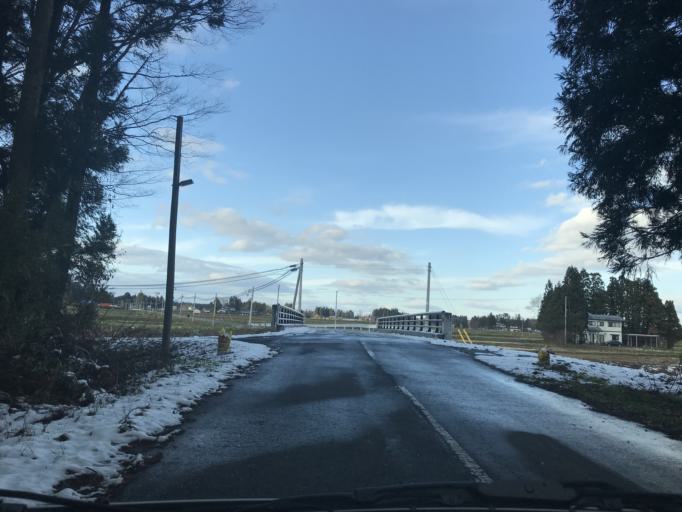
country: JP
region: Iwate
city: Kitakami
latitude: 39.2130
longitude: 141.0493
